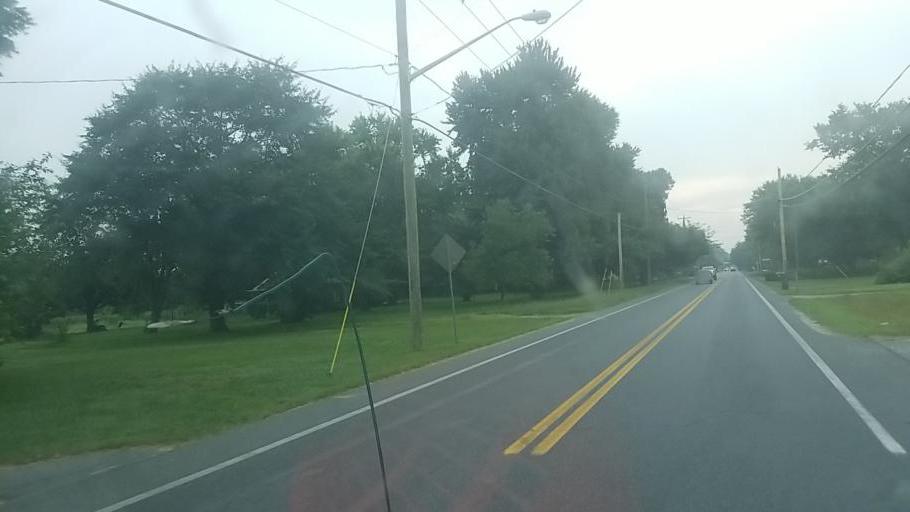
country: US
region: Maryland
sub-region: Wicomico County
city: Salisbury
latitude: 38.3733
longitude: -75.5470
